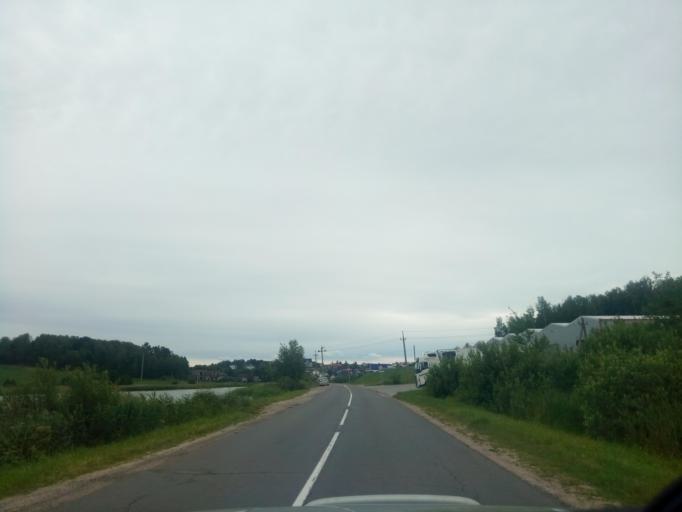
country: BY
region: Minsk
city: Zhdanovichy
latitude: 53.9344
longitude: 27.3863
